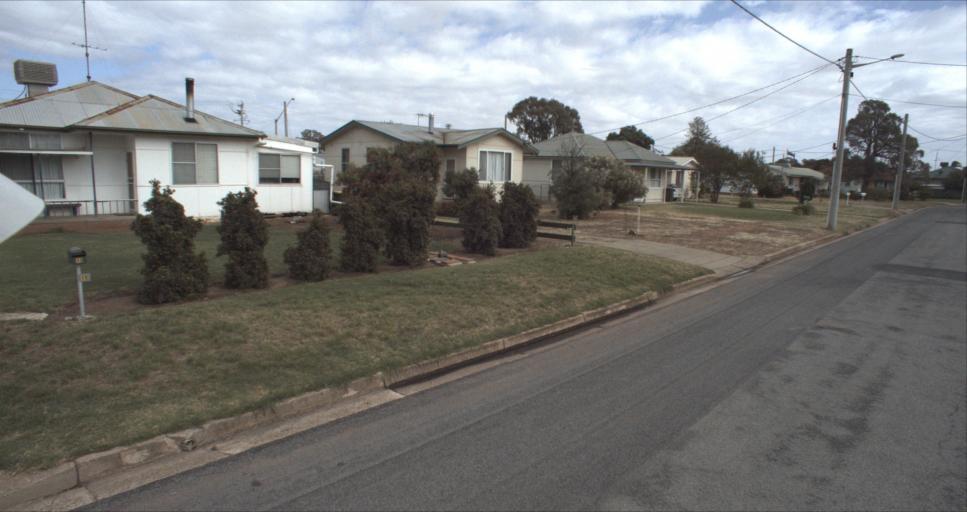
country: AU
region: New South Wales
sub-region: Leeton
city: Leeton
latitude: -34.5651
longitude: 146.3940
